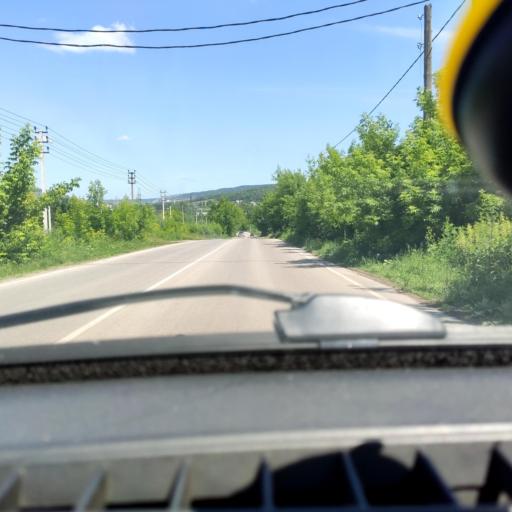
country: RU
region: Samara
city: Zhigulevsk
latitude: 53.3829
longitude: 49.5028
